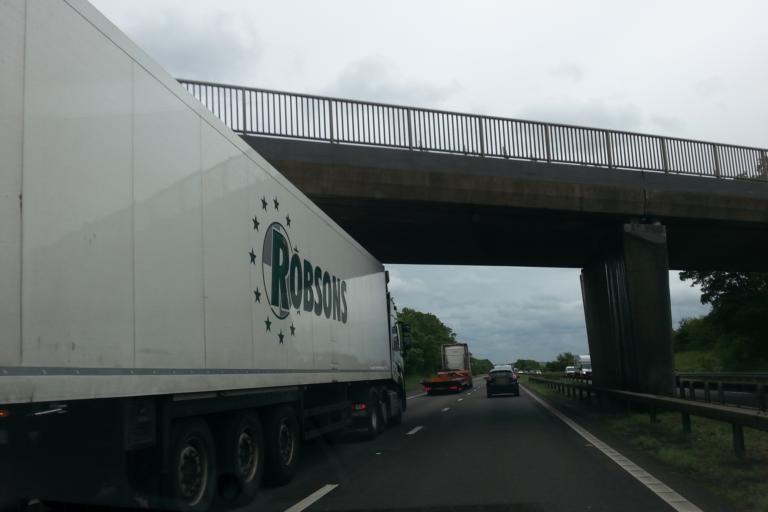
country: GB
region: England
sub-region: Doncaster
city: Tickhill
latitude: 53.4502
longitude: -1.1110
